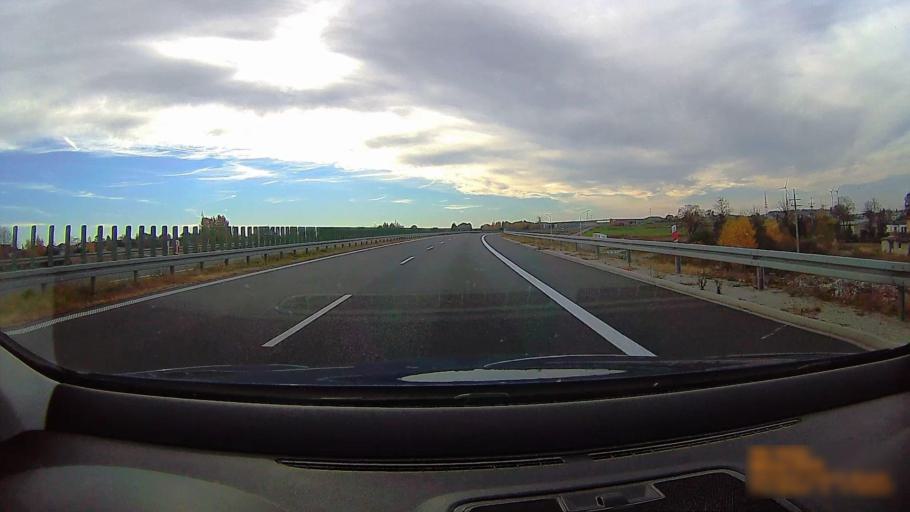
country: PL
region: Greater Poland Voivodeship
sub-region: Powiat ostrowski
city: Ostrow Wielkopolski
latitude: 51.6412
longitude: 17.8758
